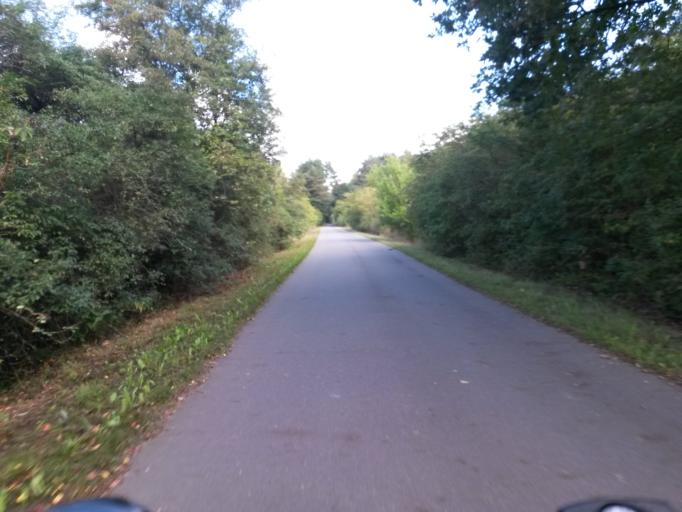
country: DE
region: Brandenburg
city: Templin
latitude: 53.2043
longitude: 13.5159
